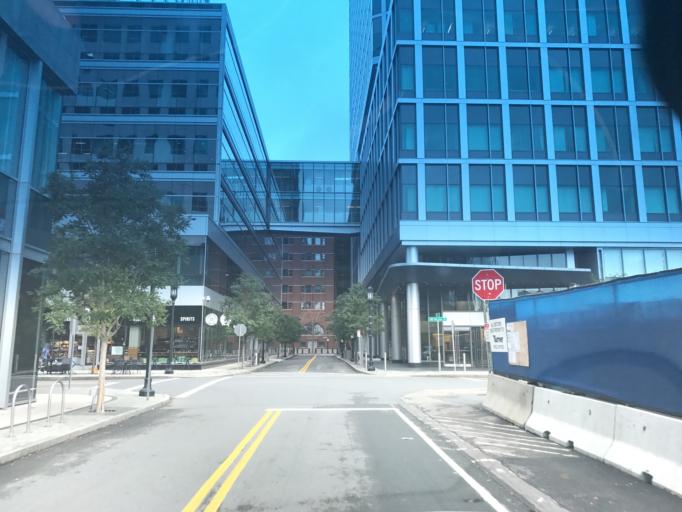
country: US
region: Massachusetts
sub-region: Suffolk County
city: Boston
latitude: 42.3535
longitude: -71.0452
